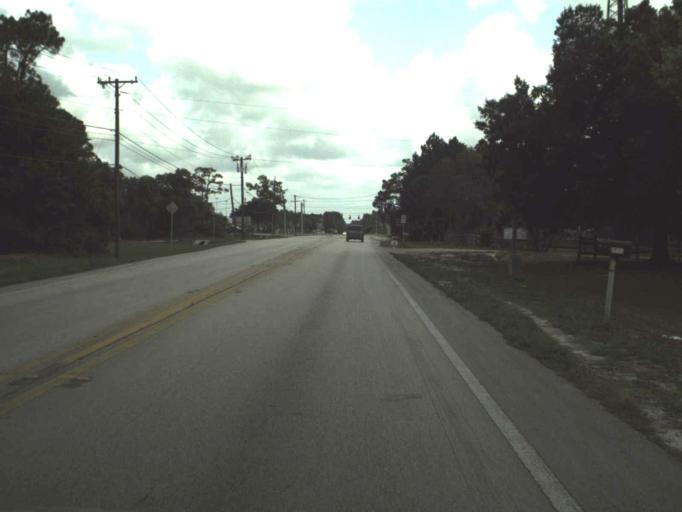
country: US
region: Florida
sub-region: Volusia County
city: Samsula-Spruce Creek
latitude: 29.0081
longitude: -81.0693
